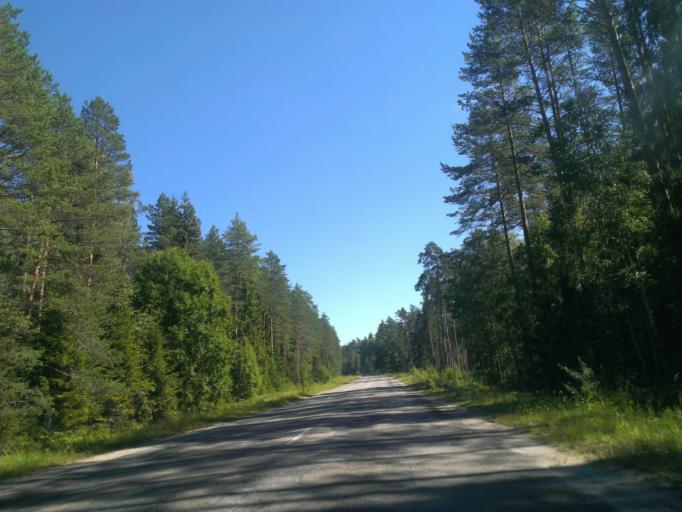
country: LV
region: Incukalns
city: Incukalns
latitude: 57.0306
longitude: 24.7108
